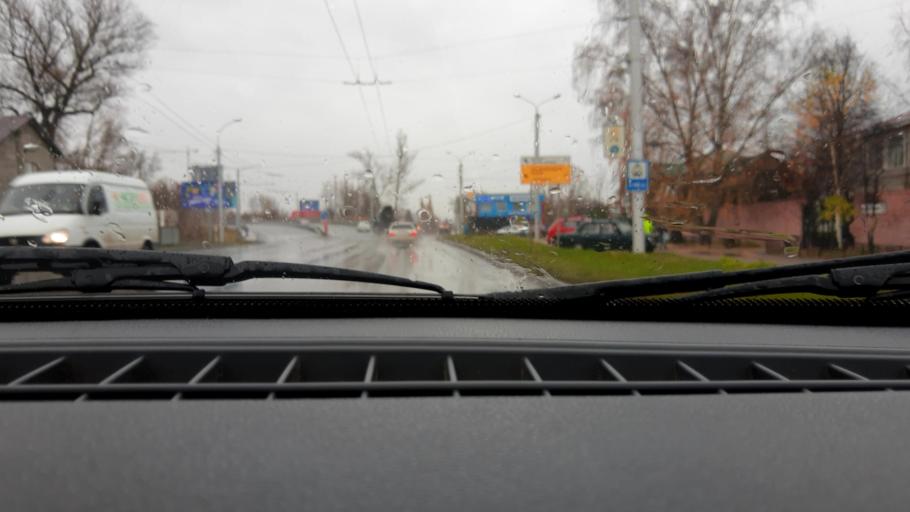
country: RU
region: Bashkortostan
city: Mikhaylovka
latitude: 54.7775
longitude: 55.8907
